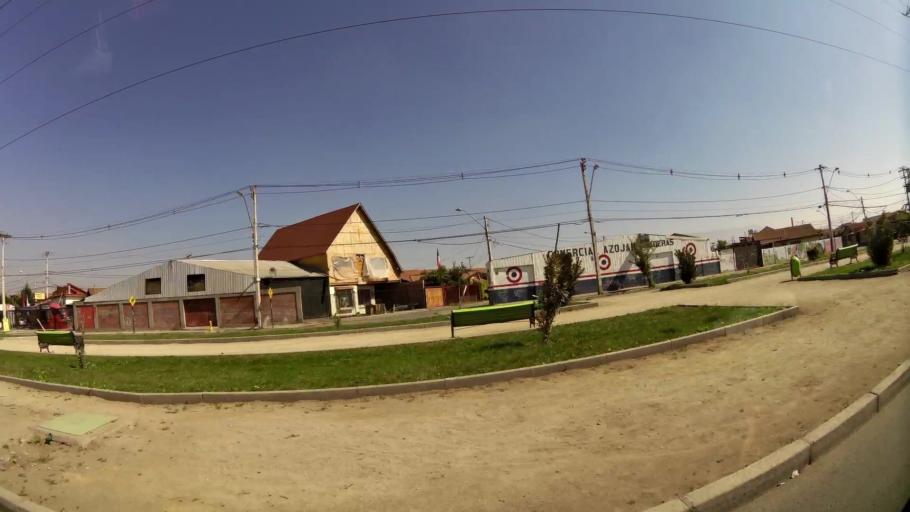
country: CL
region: Santiago Metropolitan
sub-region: Provincia de Santiago
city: Lo Prado
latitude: -33.3489
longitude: -70.7421
